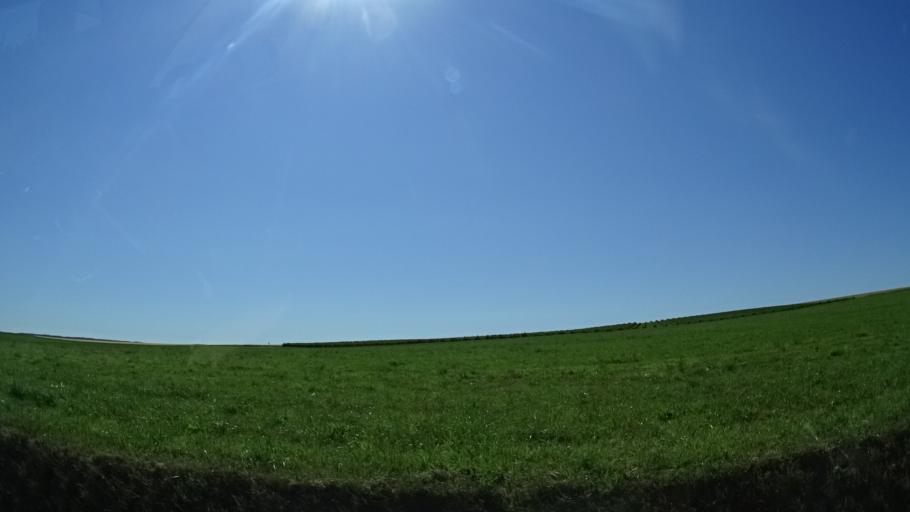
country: DE
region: Bavaria
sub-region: Regierungsbezirk Unterfranken
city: Eichenbuhl
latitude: 49.7104
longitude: 9.3625
